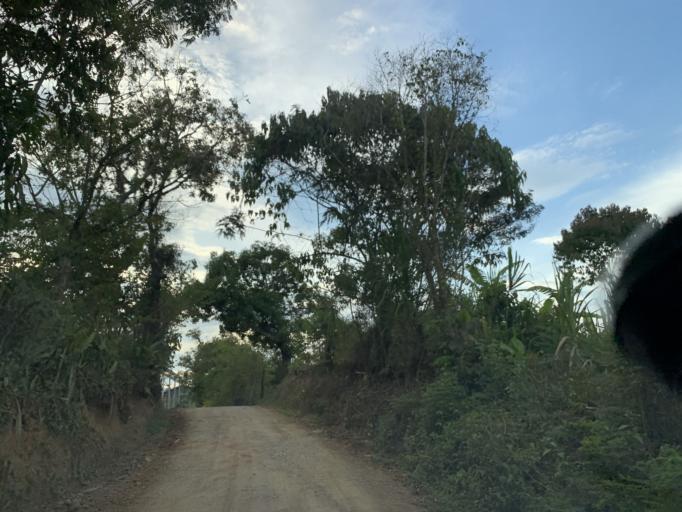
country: CO
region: Boyaca
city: Santana
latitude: 6.0821
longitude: -73.4933
